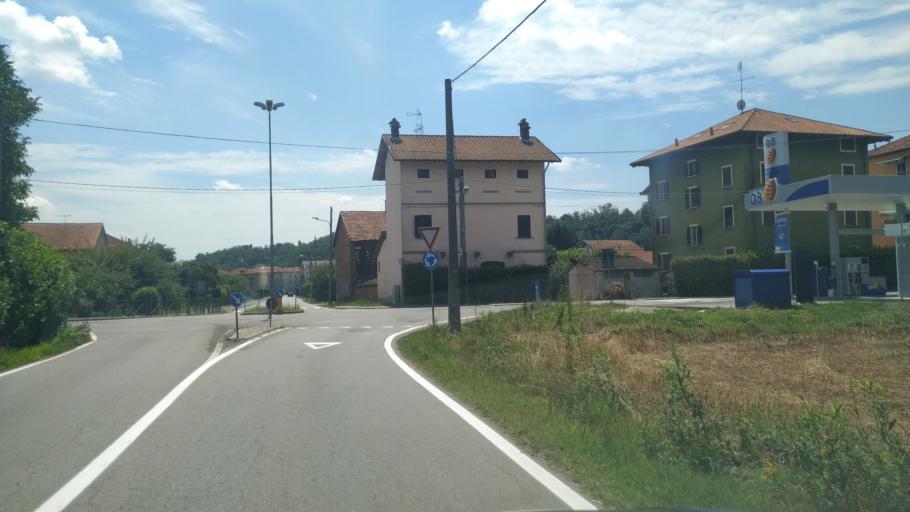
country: IT
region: Piedmont
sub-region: Provincia di Novara
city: Borgomanero
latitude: 45.7031
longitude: 8.4470
